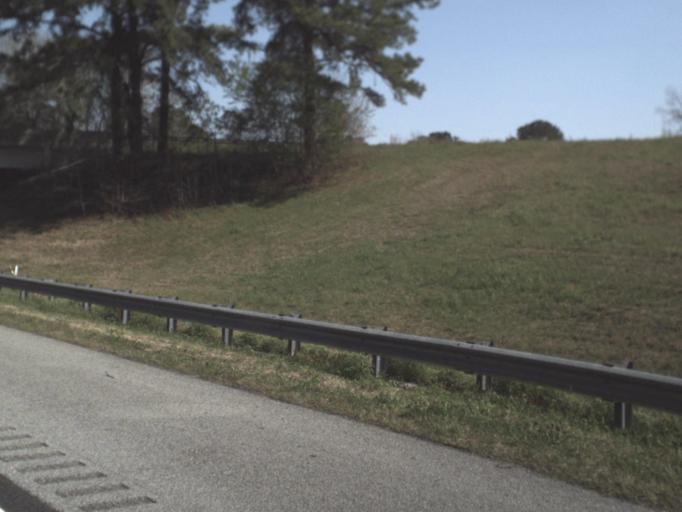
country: US
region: Florida
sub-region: Jackson County
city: Sneads
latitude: 30.6363
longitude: -84.9457
